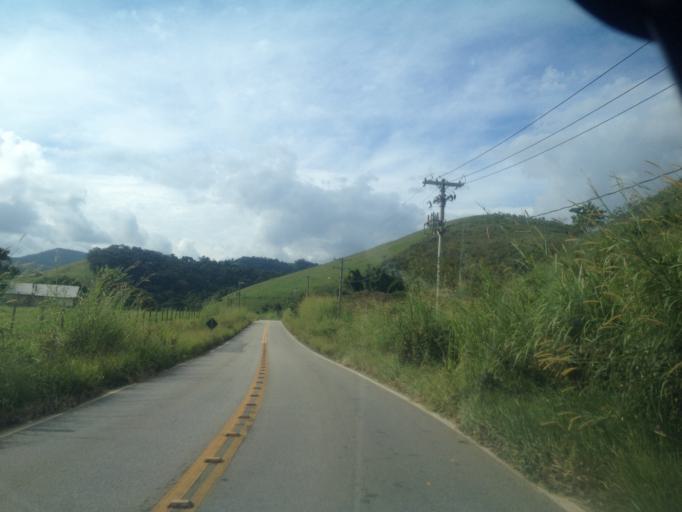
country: BR
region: Rio de Janeiro
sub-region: Quatis
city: Quatis
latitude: -22.3554
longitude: -44.2454
